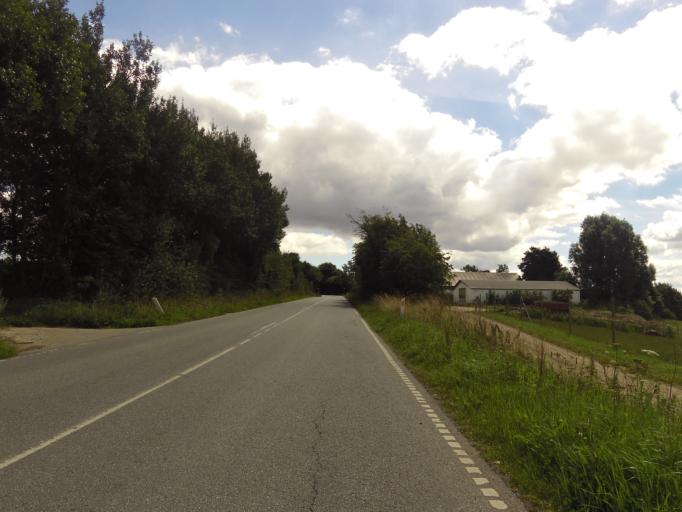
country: DK
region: South Denmark
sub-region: Haderslev Kommune
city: Haderslev
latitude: 55.2588
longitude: 9.4437
